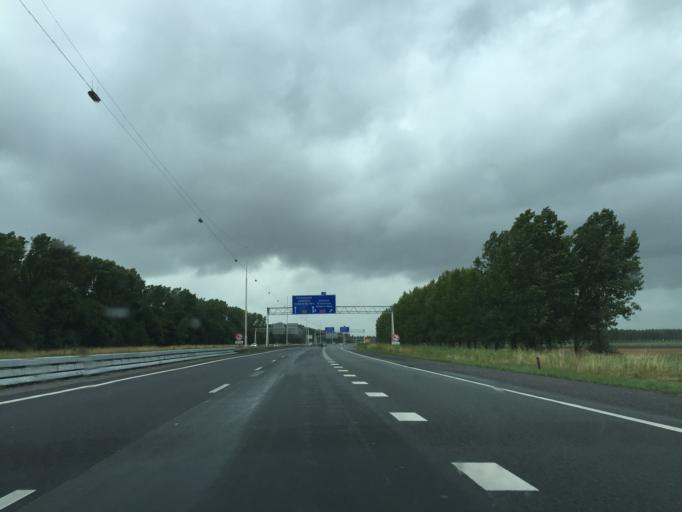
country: NL
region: Flevoland
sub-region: Gemeente Almere
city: Almere Stad
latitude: 52.3747
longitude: 5.2895
